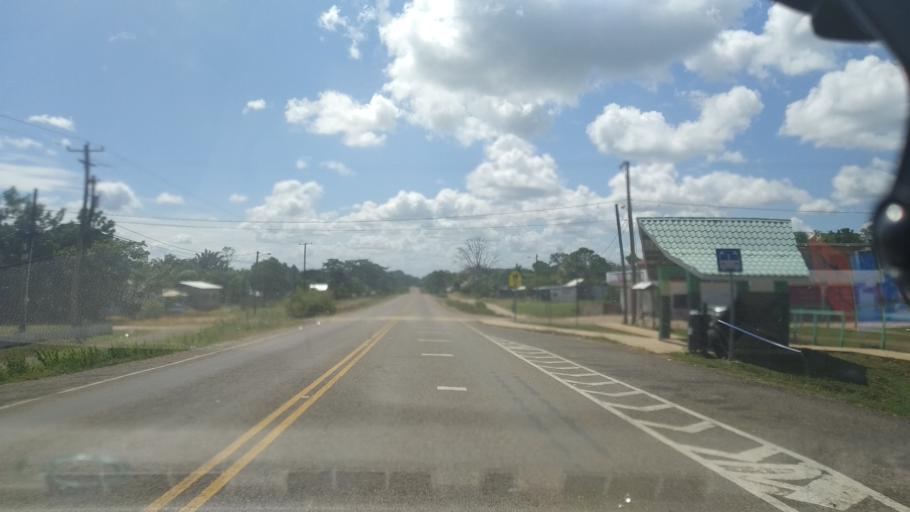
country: BZ
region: Cayo
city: Belmopan
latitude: 17.1550
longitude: -88.7454
